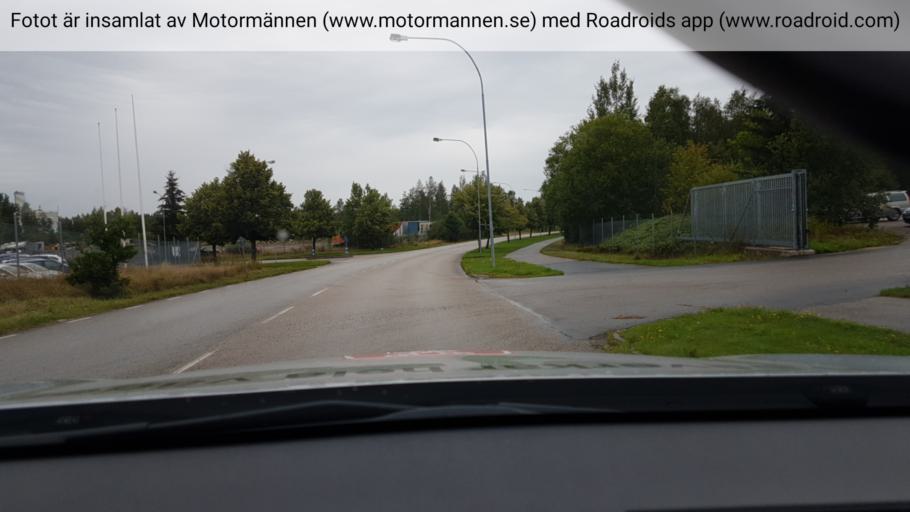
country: SE
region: Vaestra Goetaland
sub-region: Trollhattan
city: Trollhattan
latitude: 58.3434
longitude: 12.2541
